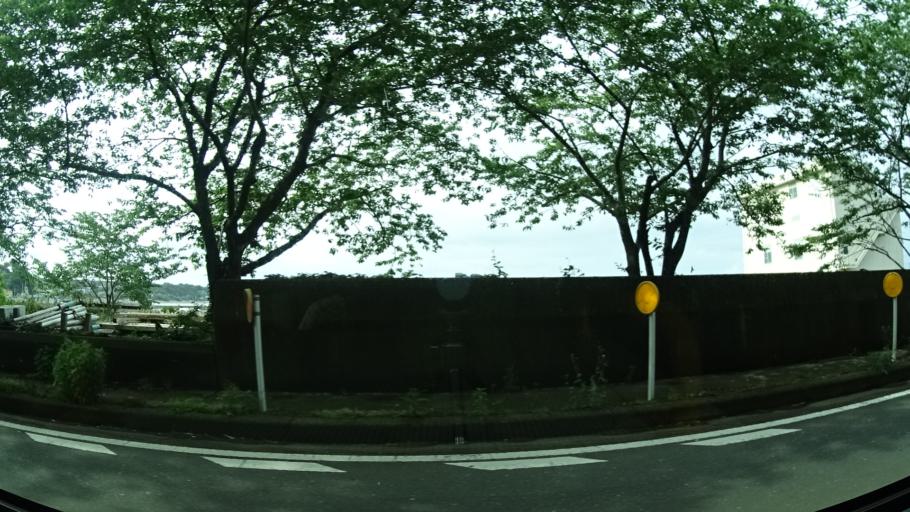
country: JP
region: Kanagawa
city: Miura
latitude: 35.1583
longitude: 139.6659
